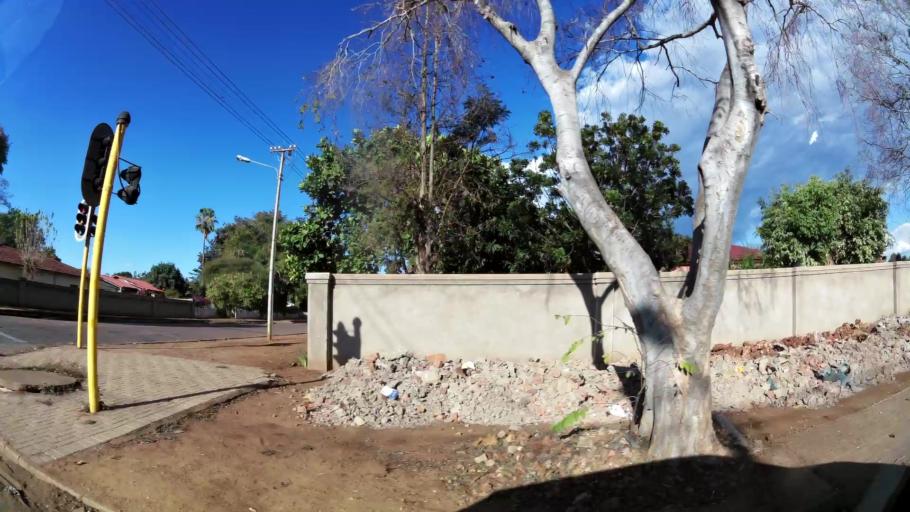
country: ZA
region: Limpopo
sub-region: Waterberg District Municipality
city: Mokopane
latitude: -24.1826
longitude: 29.0000
